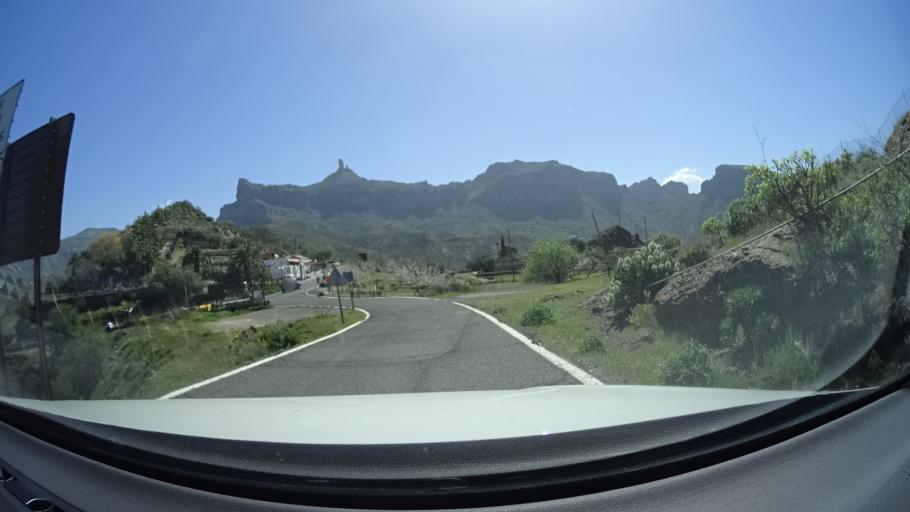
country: ES
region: Canary Islands
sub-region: Provincia de Las Palmas
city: Tejeda
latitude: 27.9882
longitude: -15.6316
